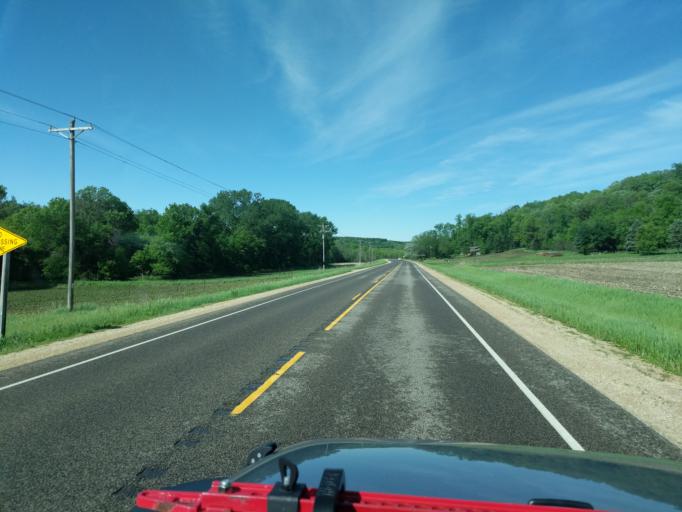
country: US
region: Wisconsin
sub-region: Pierce County
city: River Falls
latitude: 44.8519
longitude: -92.5480
